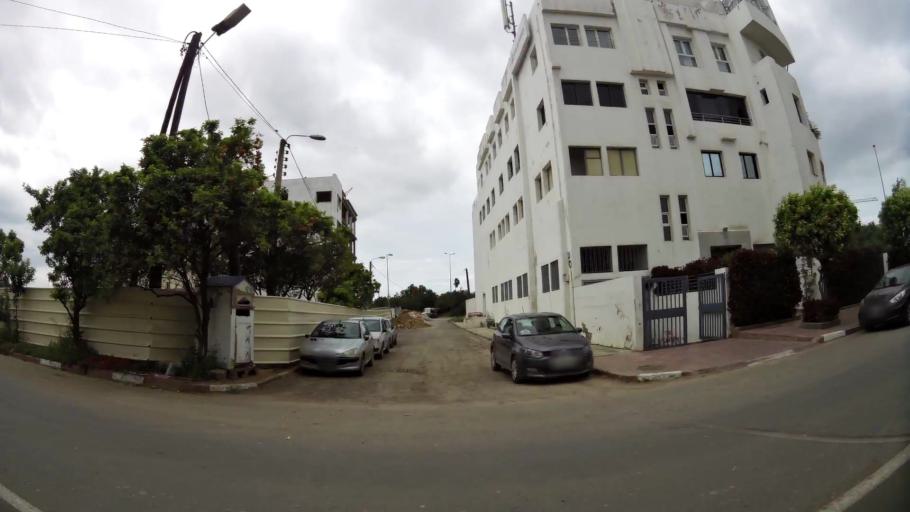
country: MA
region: Grand Casablanca
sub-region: Casablanca
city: Casablanca
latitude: 33.5506
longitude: -7.6343
